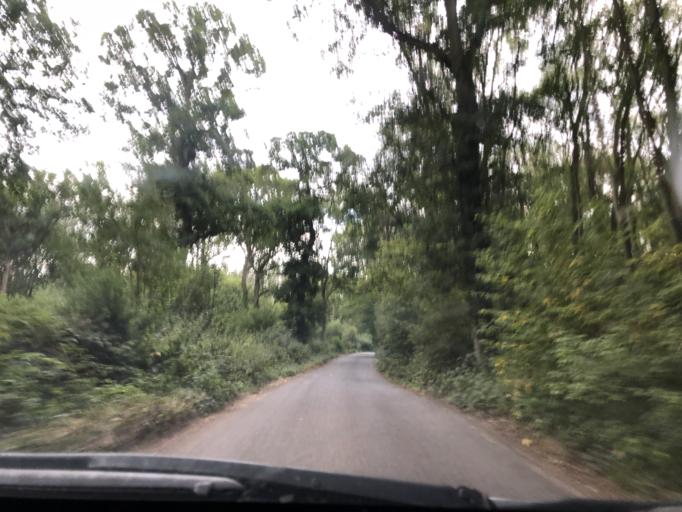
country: GB
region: England
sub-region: Kent
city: Sevenoaks
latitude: 51.2393
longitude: 0.2207
